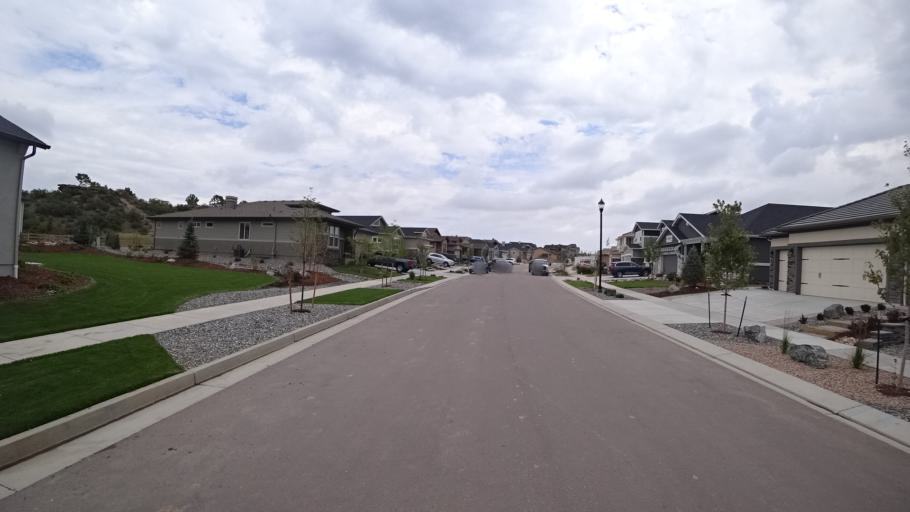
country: US
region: Colorado
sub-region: El Paso County
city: Gleneagle
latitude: 39.0091
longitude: -104.7890
